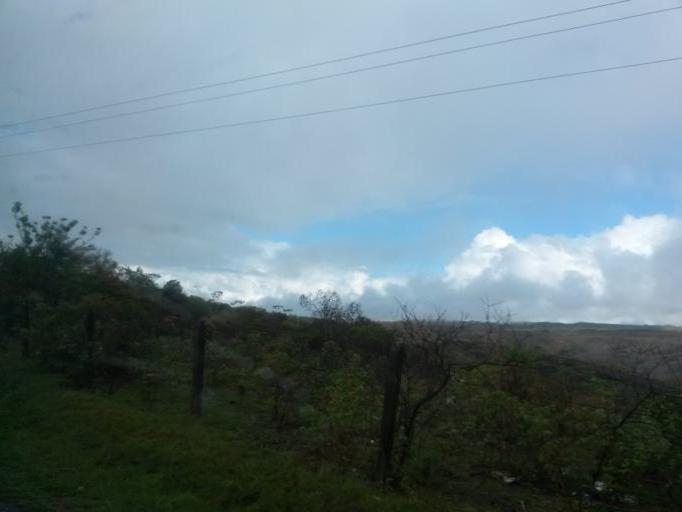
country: CO
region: Cauca
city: El Bordo
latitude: 2.1492
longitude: -76.9209
